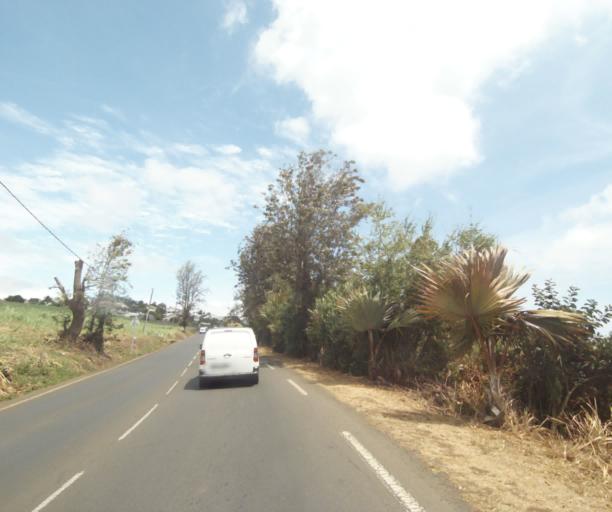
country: RE
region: Reunion
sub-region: Reunion
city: Trois-Bassins
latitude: -21.0706
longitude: 55.2672
